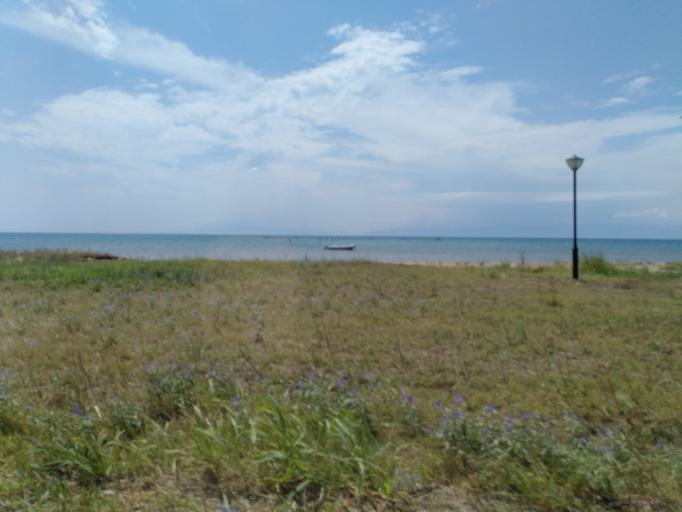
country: GR
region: Central Macedonia
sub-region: Nomos Thessalonikis
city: Nea Michaniona
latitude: 40.4304
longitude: 22.8720
